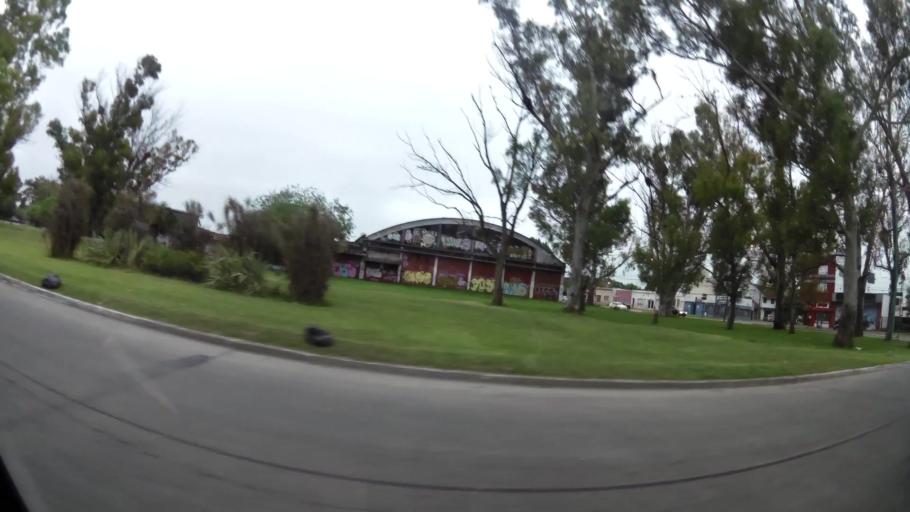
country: AR
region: Buenos Aires
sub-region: Partido de La Plata
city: La Plata
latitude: -34.8970
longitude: -57.9745
